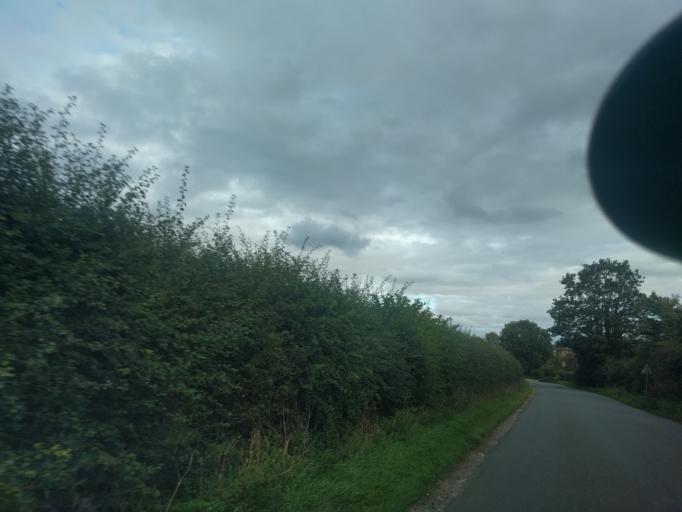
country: GB
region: England
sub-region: Wiltshire
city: Lacock
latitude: 51.4222
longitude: -2.1370
